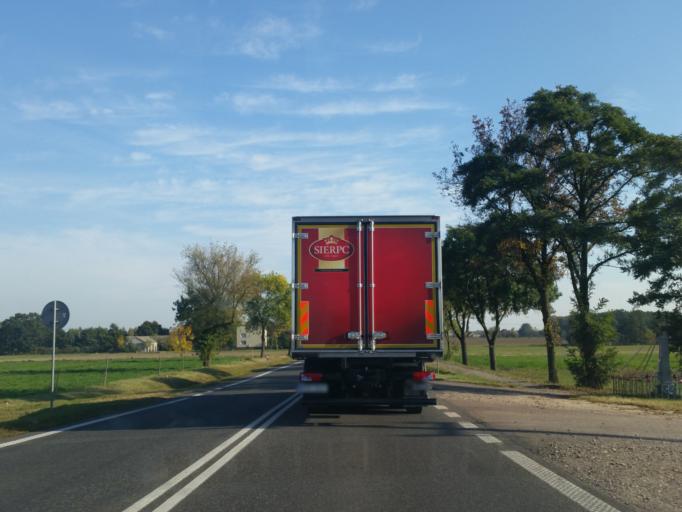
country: PL
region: Masovian Voivodeship
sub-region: Powiat sierpecki
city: Rosciszewo
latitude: 52.8352
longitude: 19.7417
